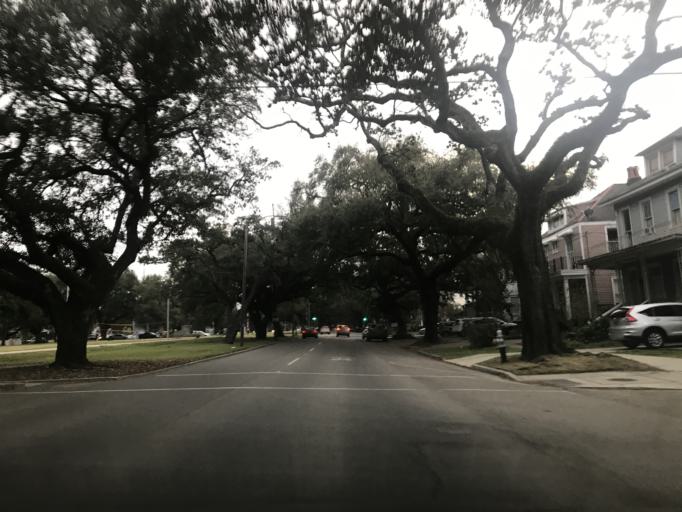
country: US
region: Louisiana
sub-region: Orleans Parish
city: New Orleans
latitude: 29.9686
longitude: -90.0958
